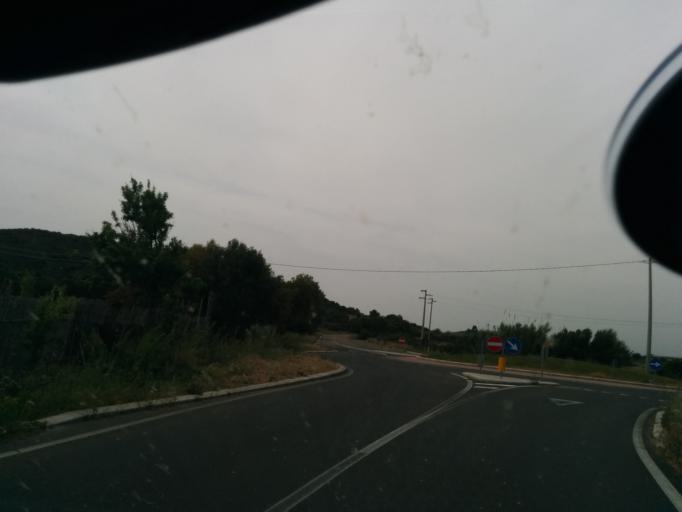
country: IT
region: Sardinia
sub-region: Provincia di Carbonia-Iglesias
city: Sant'Antioco
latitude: 39.0403
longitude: 8.4544
